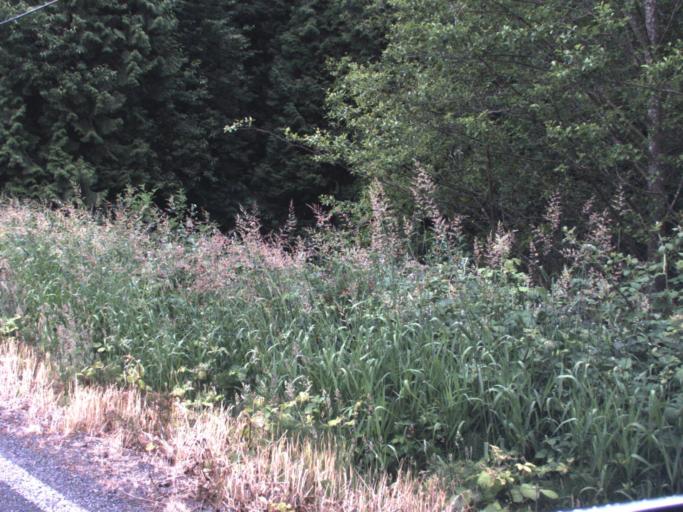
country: US
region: Washington
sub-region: Whatcom County
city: Birch Bay
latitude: 48.9297
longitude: -122.7263
